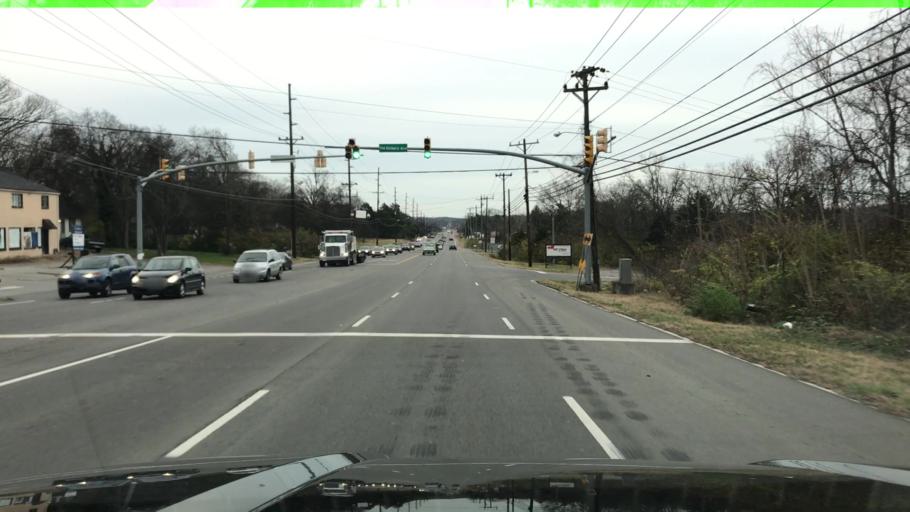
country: US
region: Tennessee
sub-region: Rutherford County
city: La Vergne
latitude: 36.0397
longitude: -86.6033
